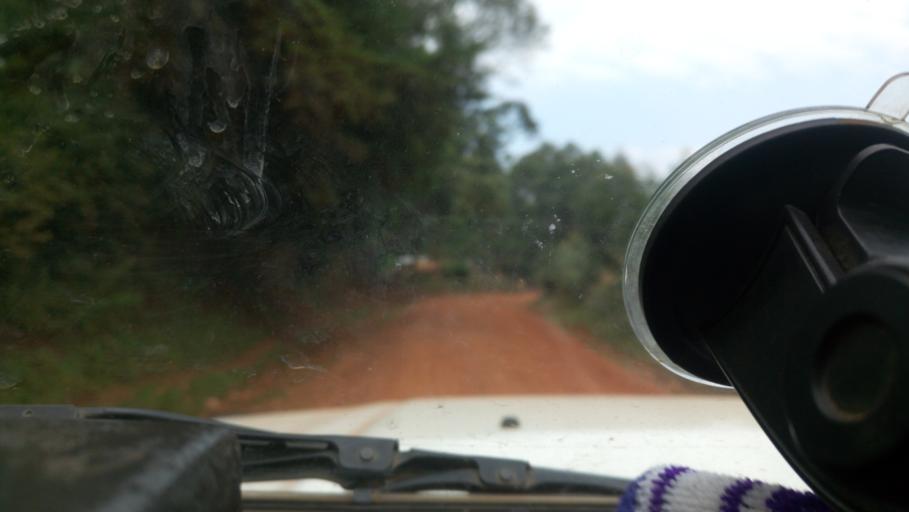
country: KE
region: Kericho
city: Litein
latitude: -0.6173
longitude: 35.2141
